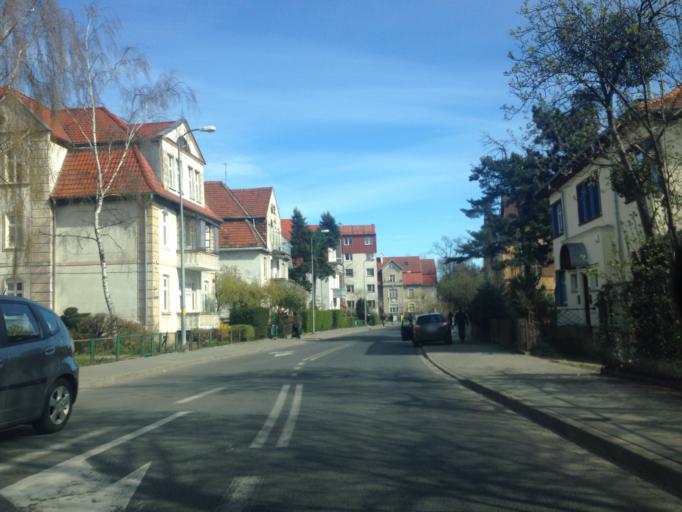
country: PL
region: Pomeranian Voivodeship
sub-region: Gdansk
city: Gdansk
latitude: 54.3743
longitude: 18.6132
